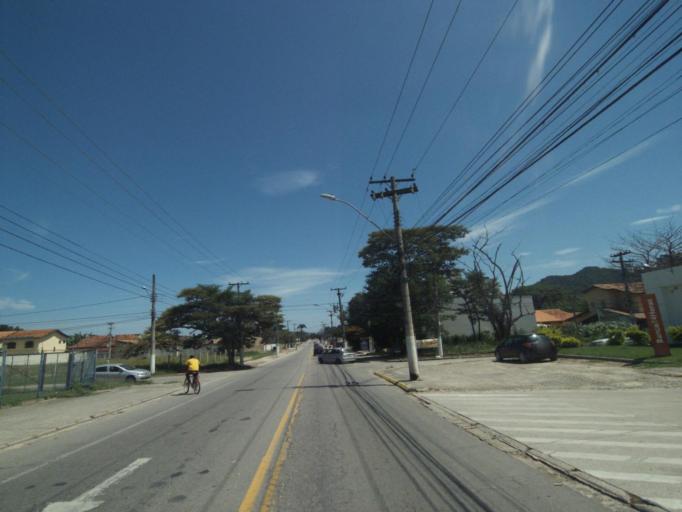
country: BR
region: Rio de Janeiro
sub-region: Niteroi
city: Niteroi
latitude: -22.9311
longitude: -43.0174
